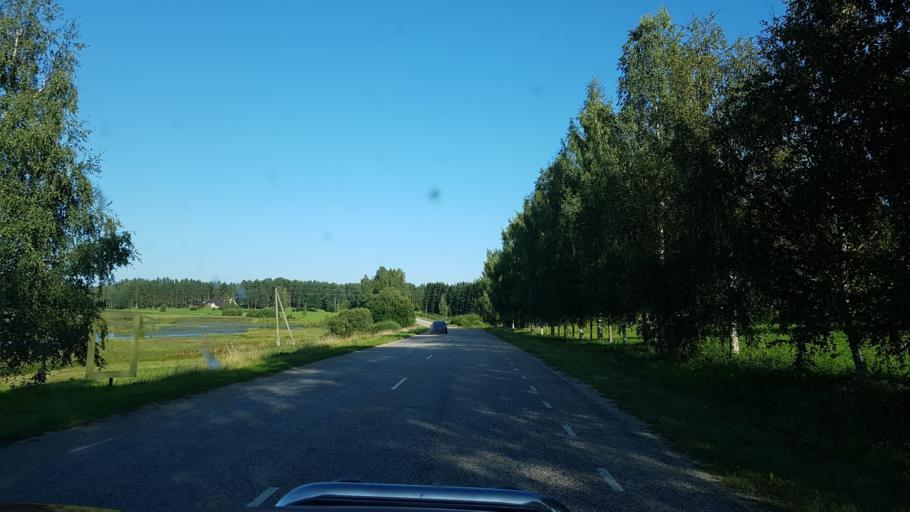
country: EE
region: Vorumaa
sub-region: Voru linn
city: Voru
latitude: 57.8146
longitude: 27.3085
